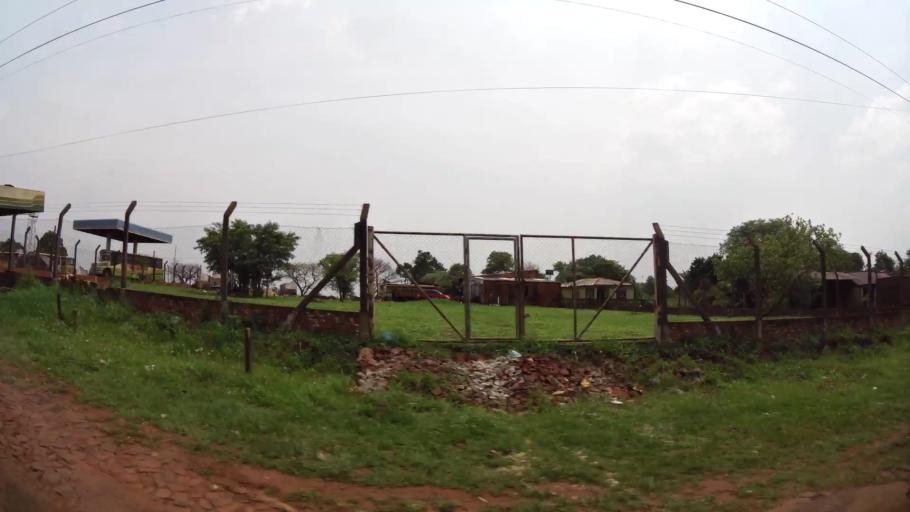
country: BR
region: Parana
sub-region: Foz Do Iguacu
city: Foz do Iguacu
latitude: -25.5758
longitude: -54.6030
